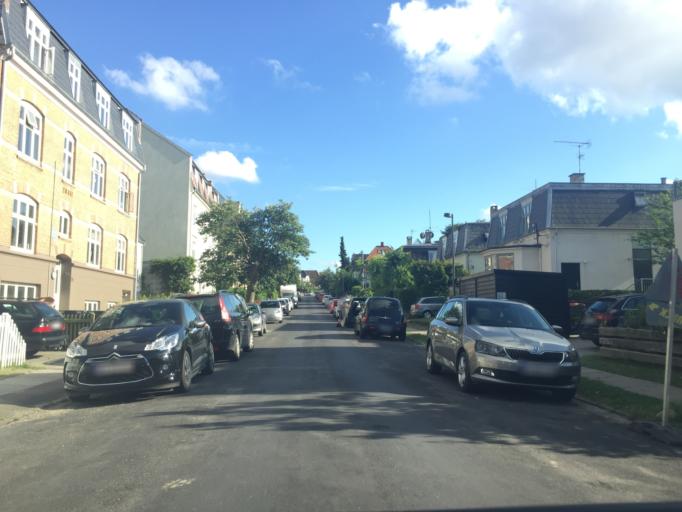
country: DK
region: Capital Region
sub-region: Kobenhavn
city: Vanlose
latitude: 55.7042
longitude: 12.5051
